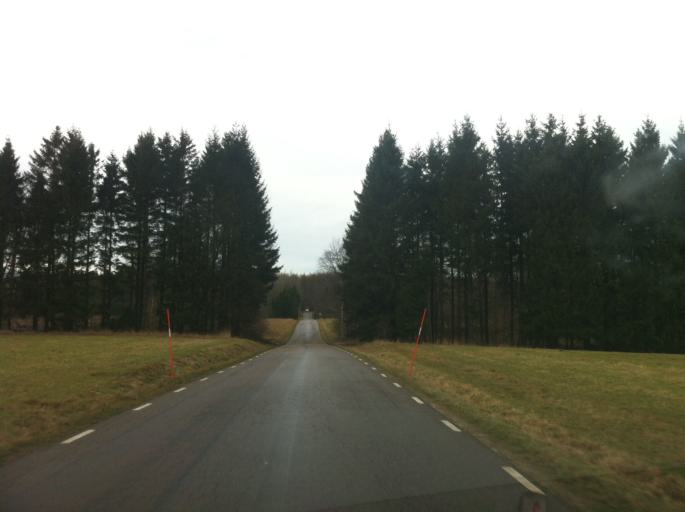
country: SE
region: Skane
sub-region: Svalovs Kommun
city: Kagerod
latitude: 56.0560
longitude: 13.1062
